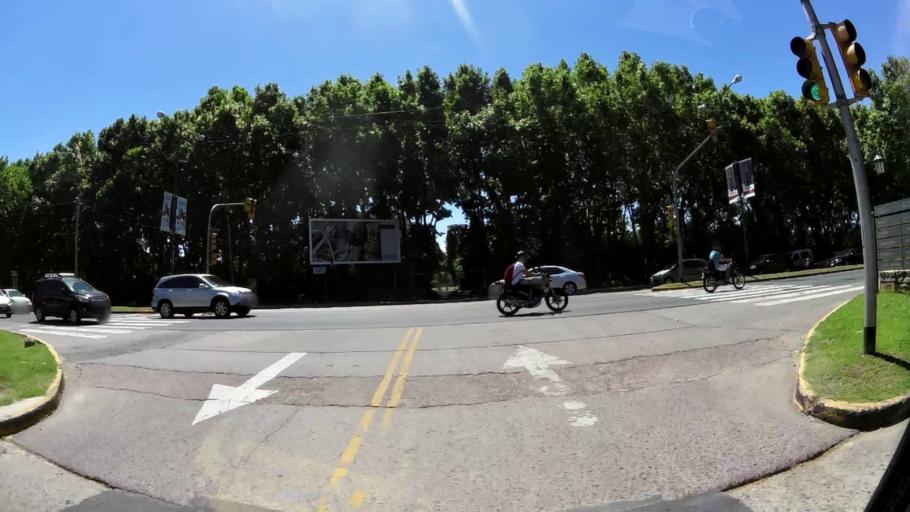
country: AR
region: Buenos Aires
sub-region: Partido de San Isidro
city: San Isidro
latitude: -34.4917
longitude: -58.5283
